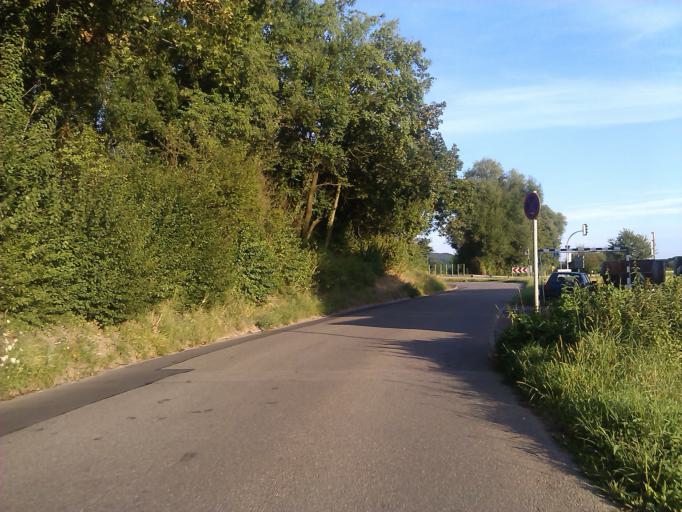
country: DE
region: Baden-Wuerttemberg
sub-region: Karlsruhe Region
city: Wiesloch
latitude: 49.2851
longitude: 8.6891
